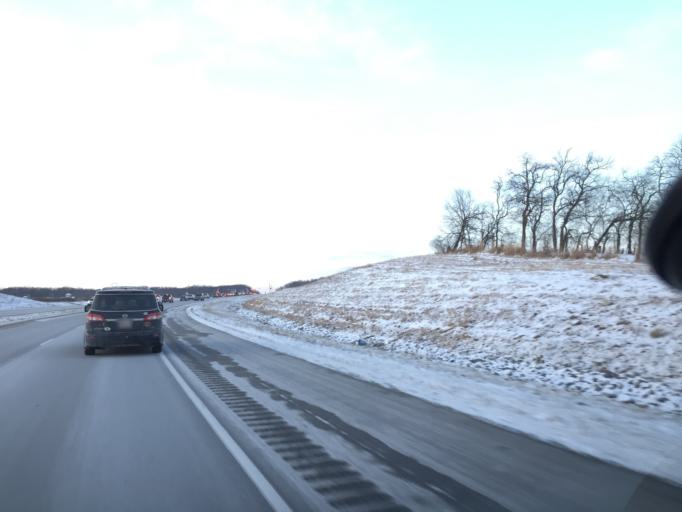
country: US
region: Indiana
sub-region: Monroe County
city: Bloomington
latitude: 39.1892
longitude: -86.5681
